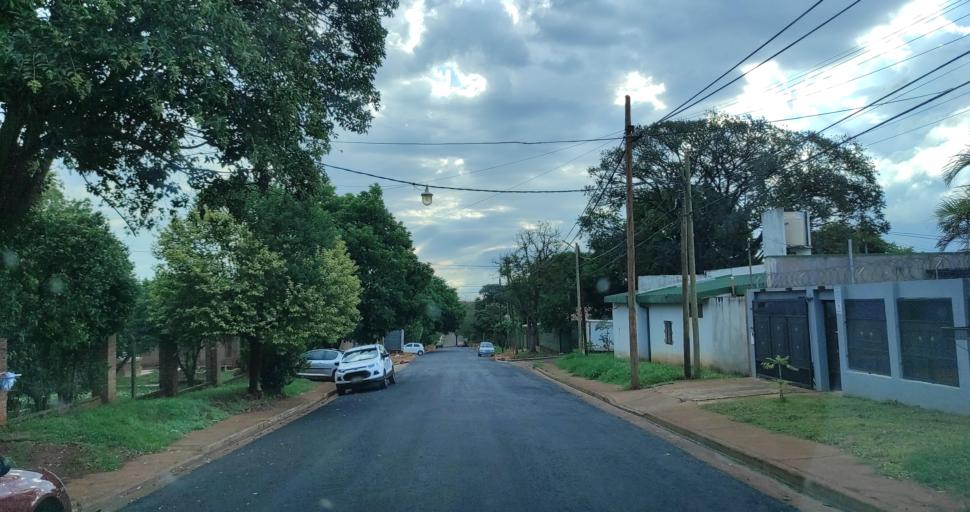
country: AR
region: Misiones
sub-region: Departamento de Capital
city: Posadas
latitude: -27.3694
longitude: -55.9298
